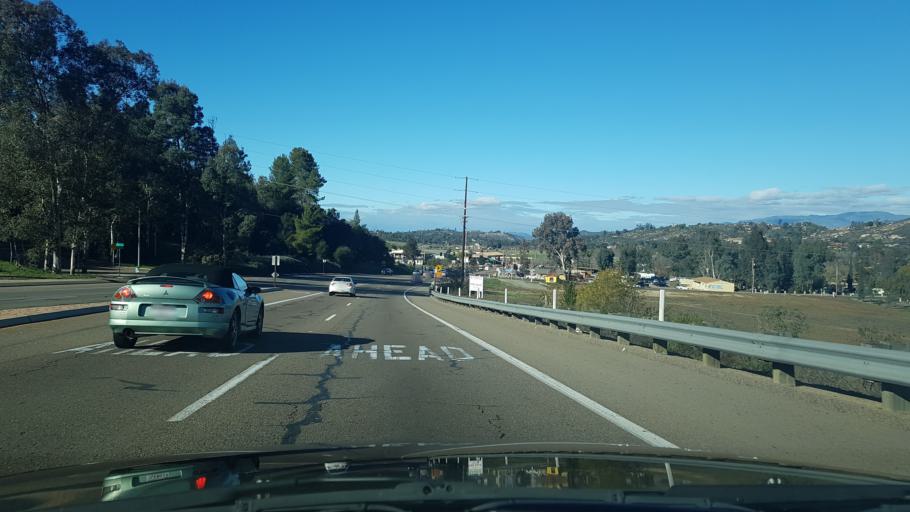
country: US
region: California
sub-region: San Diego County
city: Valley Center
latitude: 33.2036
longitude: -117.0324
